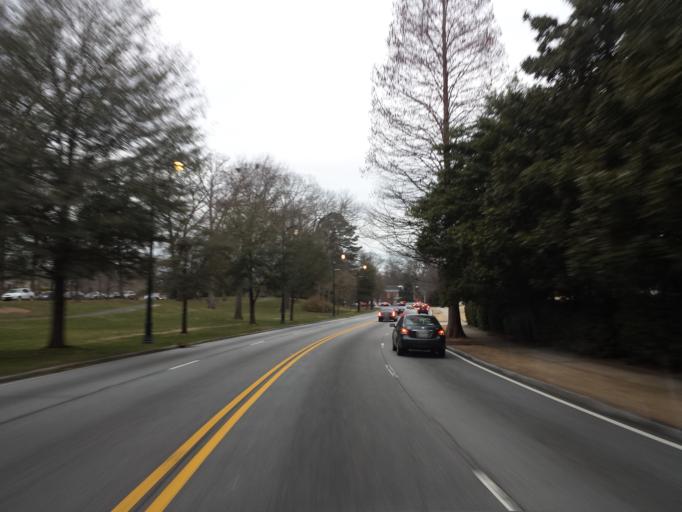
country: US
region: Georgia
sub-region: DeKalb County
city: Druid Hills
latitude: 33.7742
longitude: -84.3392
